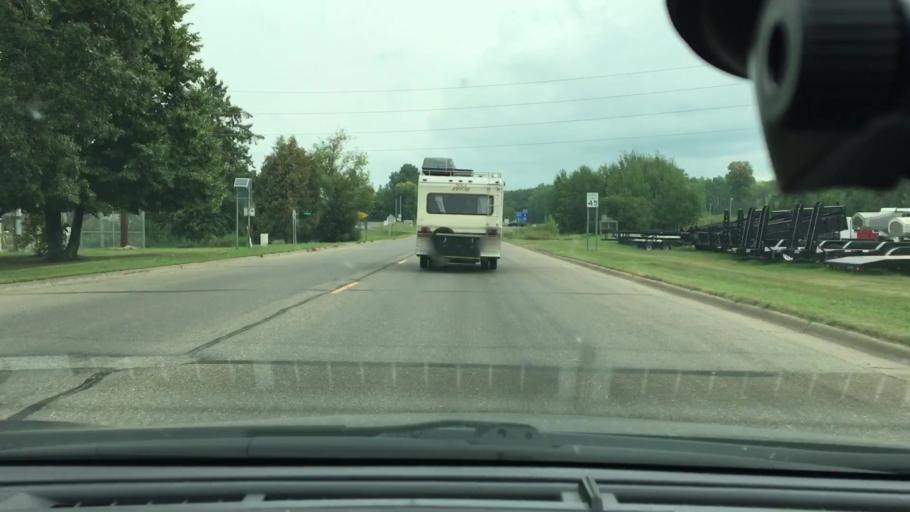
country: US
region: Minnesota
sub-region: Crow Wing County
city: Crosby
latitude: 46.4746
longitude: -93.8958
